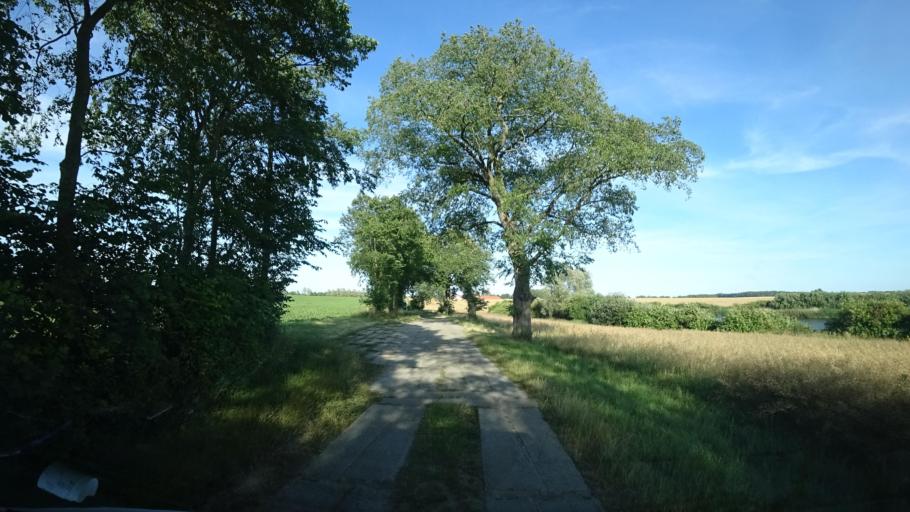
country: DE
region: Mecklenburg-Vorpommern
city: Rambin
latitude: 54.3226
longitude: 13.1895
